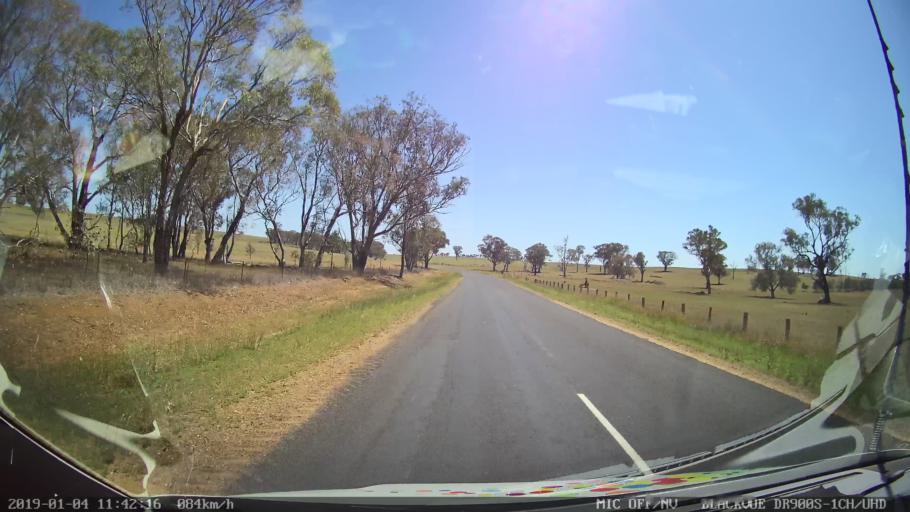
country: AU
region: New South Wales
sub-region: Cabonne
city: Molong
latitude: -32.9838
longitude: 148.7867
